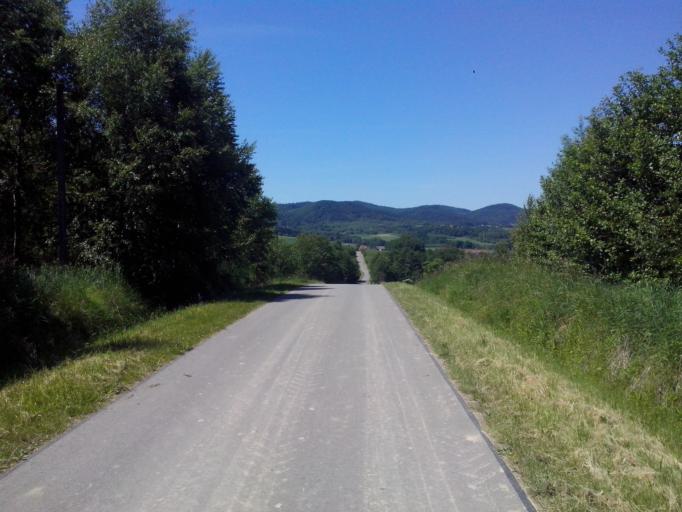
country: PL
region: Subcarpathian Voivodeship
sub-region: Powiat strzyzowski
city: Wysoka Strzyzowska
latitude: 49.8205
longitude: 21.7553
